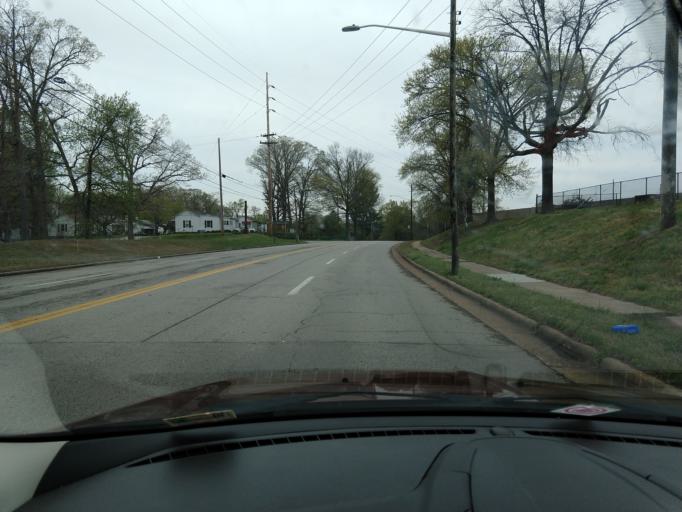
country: US
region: Virginia
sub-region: City of Danville
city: Danville
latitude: 36.5703
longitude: -79.4310
